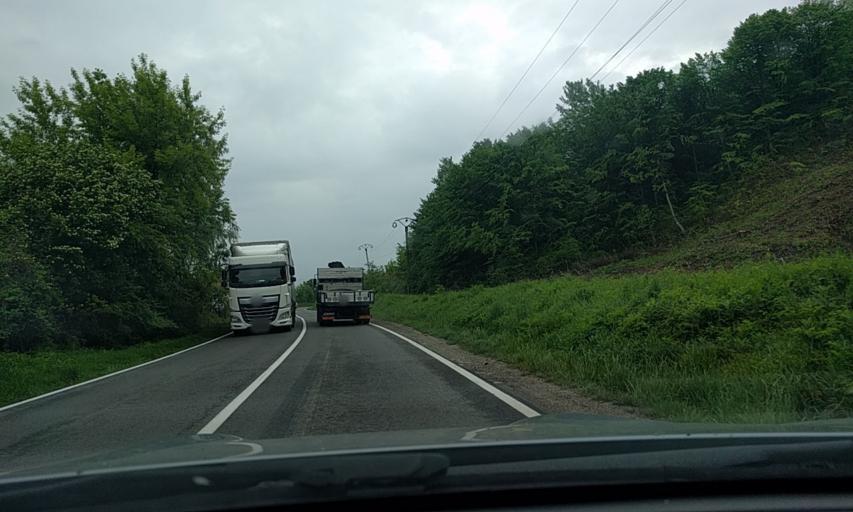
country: RO
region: Dambovita
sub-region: Comuna Vulcana-Pandele
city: Gura Vulcanei
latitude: 45.0160
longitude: 25.4093
